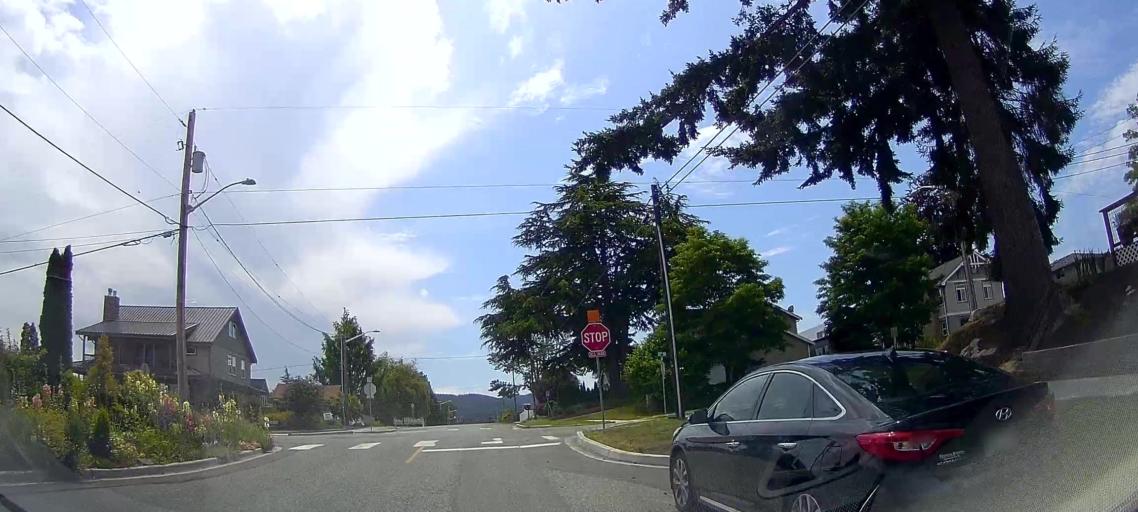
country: US
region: Washington
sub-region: Skagit County
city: Anacortes
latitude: 48.5087
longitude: -122.6205
